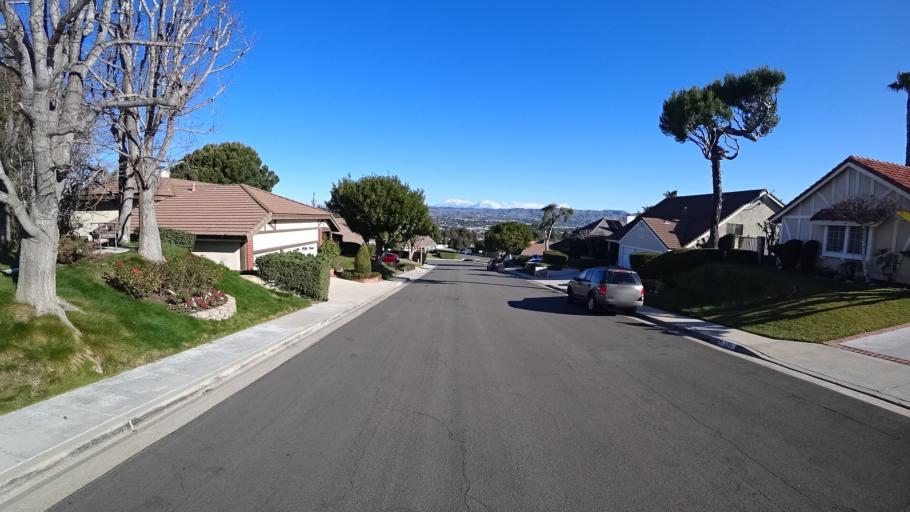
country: US
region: California
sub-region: Orange County
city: Villa Park
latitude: 33.8418
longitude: -117.7923
